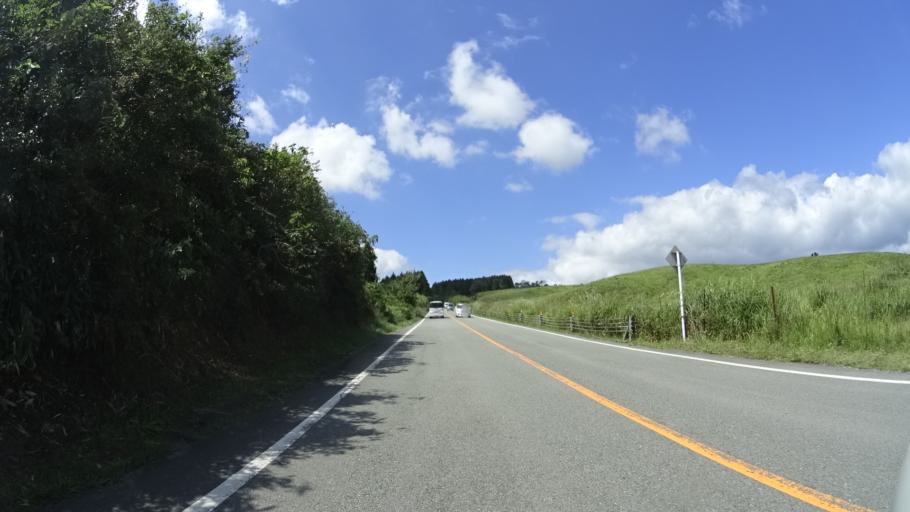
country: JP
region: Kumamoto
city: Aso
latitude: 33.0072
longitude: 131.1093
